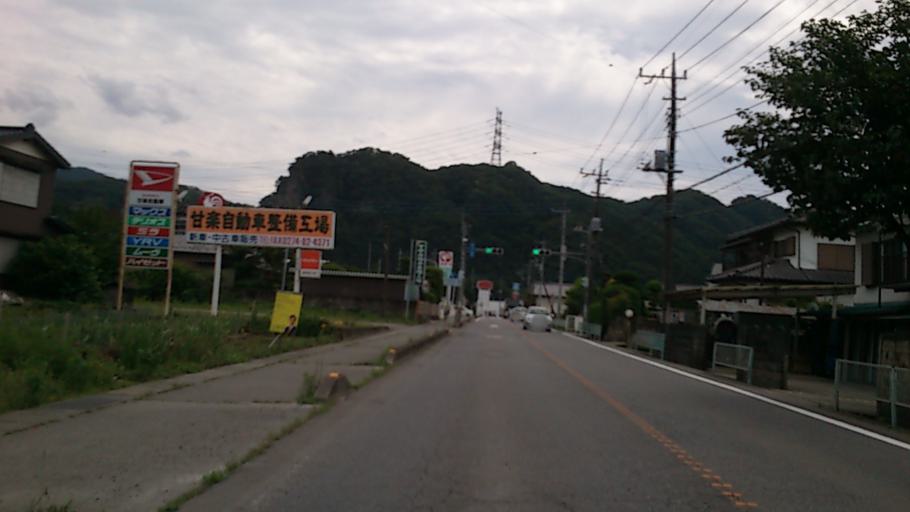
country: JP
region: Gunma
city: Tomioka
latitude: 36.2234
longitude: 138.8010
